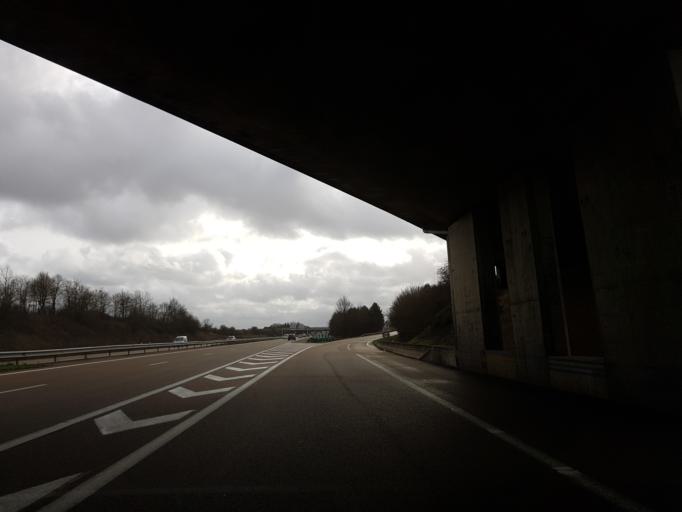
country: FR
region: Champagne-Ardenne
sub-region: Departement de la Haute-Marne
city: Rolampont
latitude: 47.9150
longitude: 5.2213
